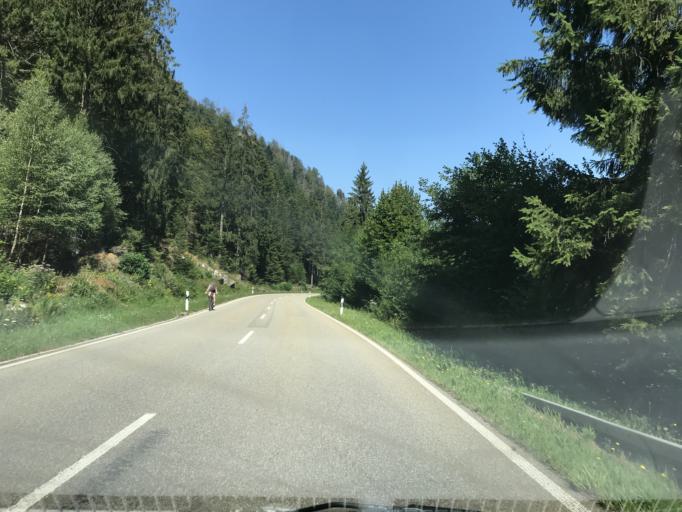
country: DE
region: Baden-Wuerttemberg
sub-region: Freiburg Region
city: Oberried
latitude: 47.9134
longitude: 7.9344
